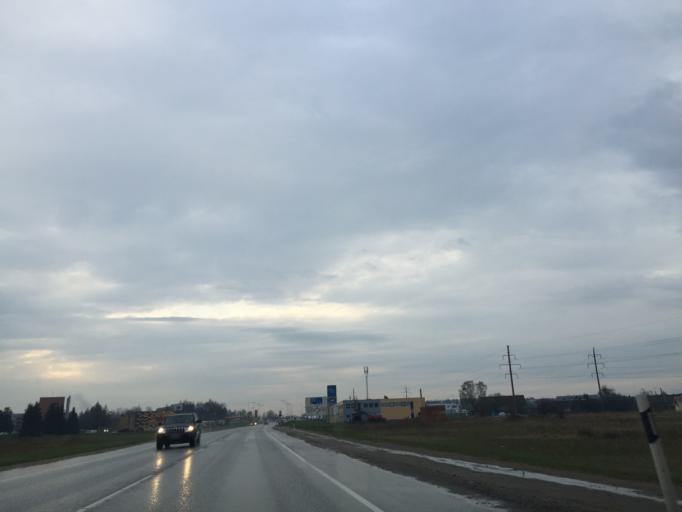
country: EE
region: Tartu
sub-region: Tartu linn
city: Tartu
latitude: 58.3504
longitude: 26.6912
